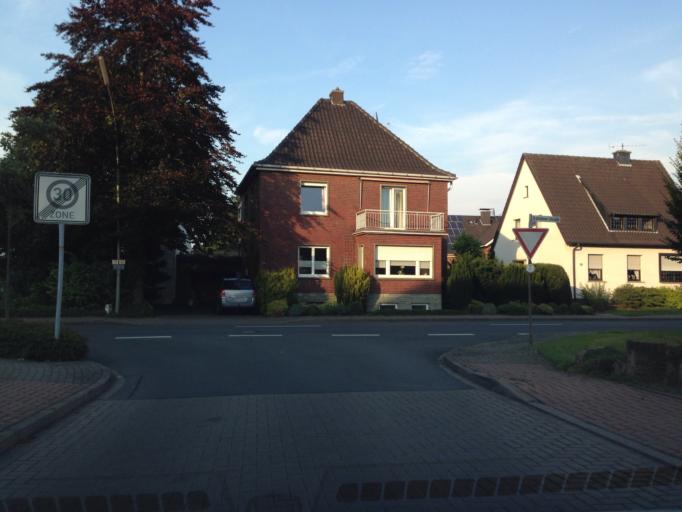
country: DE
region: North Rhine-Westphalia
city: Ludinghausen
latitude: 51.7602
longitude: 7.3959
